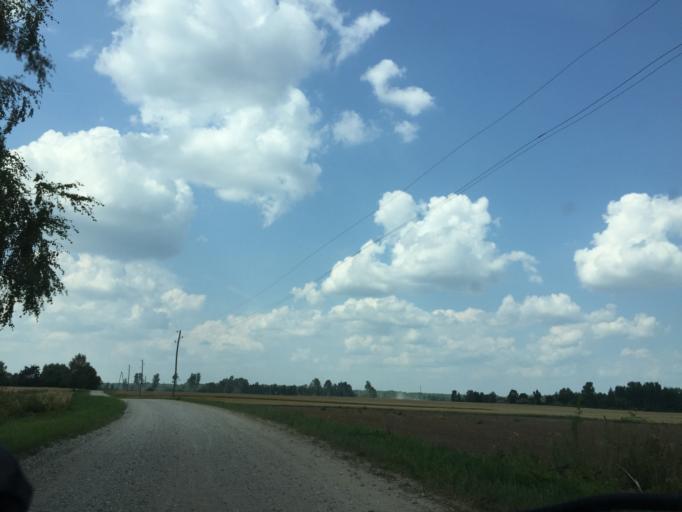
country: LT
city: Zagare
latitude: 56.3437
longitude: 23.1466
